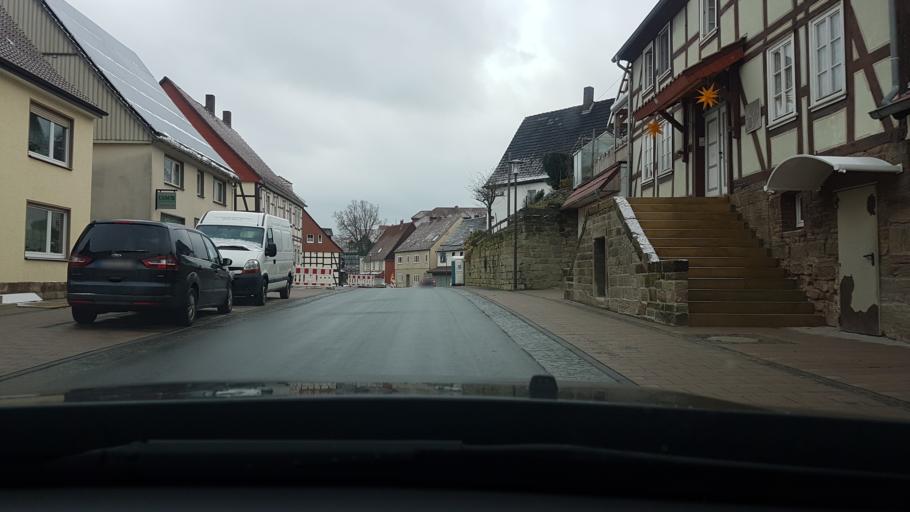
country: DE
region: Hesse
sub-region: Regierungsbezirk Kassel
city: Bad Arolsen
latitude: 51.4759
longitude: 9.0100
